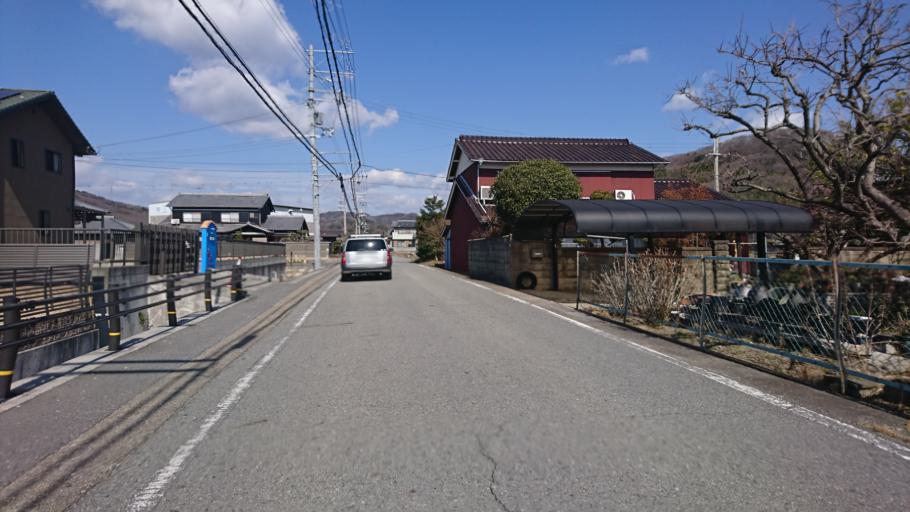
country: JP
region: Hyogo
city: Kakogawacho-honmachi
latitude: 34.8227
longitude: 134.8219
